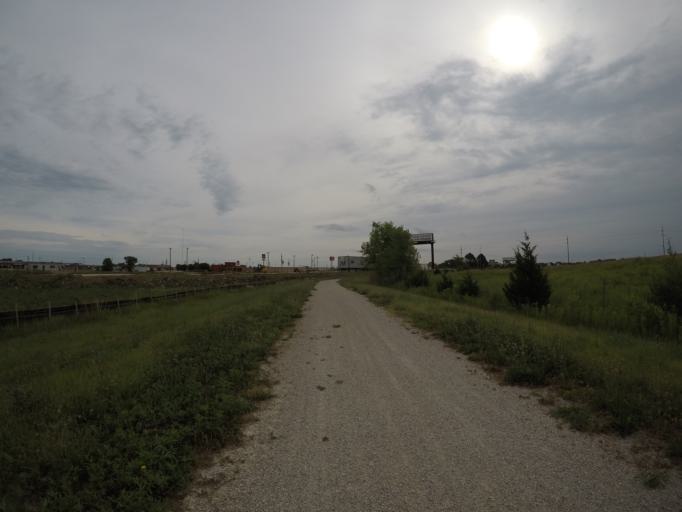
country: US
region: Kansas
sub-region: Franklin County
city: Ottawa
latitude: 38.5768
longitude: -95.2696
